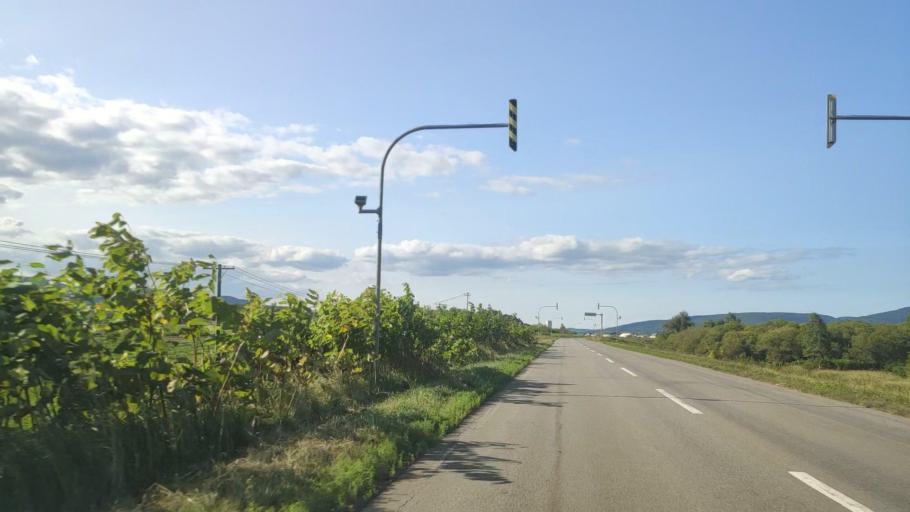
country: JP
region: Hokkaido
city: Nayoro
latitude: 44.8089
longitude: 142.0664
